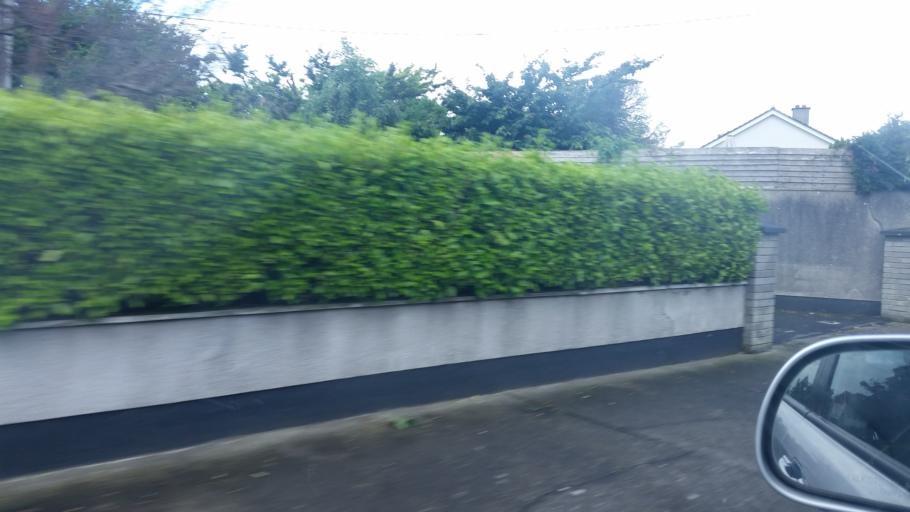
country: IE
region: Leinster
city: Portmarnock
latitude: 53.4289
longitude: -6.1324
